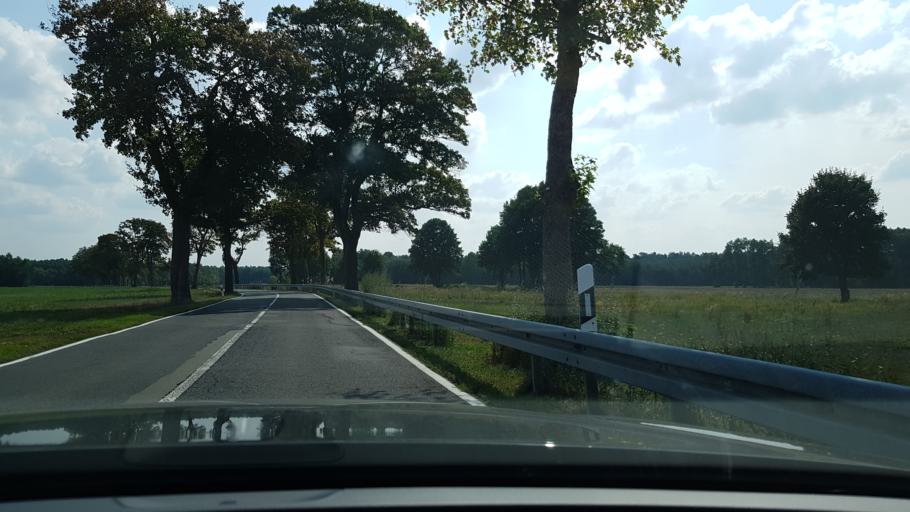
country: DE
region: Brandenburg
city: Lindow
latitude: 53.0182
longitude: 12.9757
